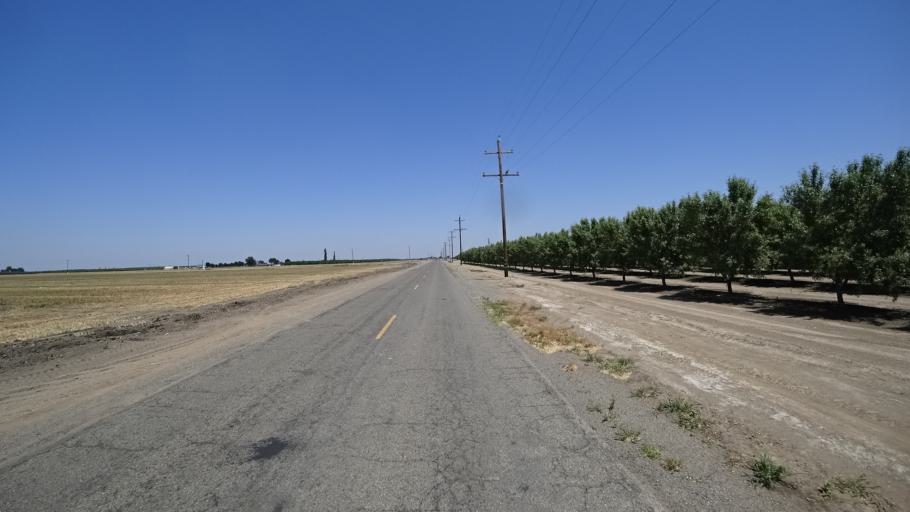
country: US
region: California
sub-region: Kings County
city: Armona
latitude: 36.3664
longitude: -119.7269
